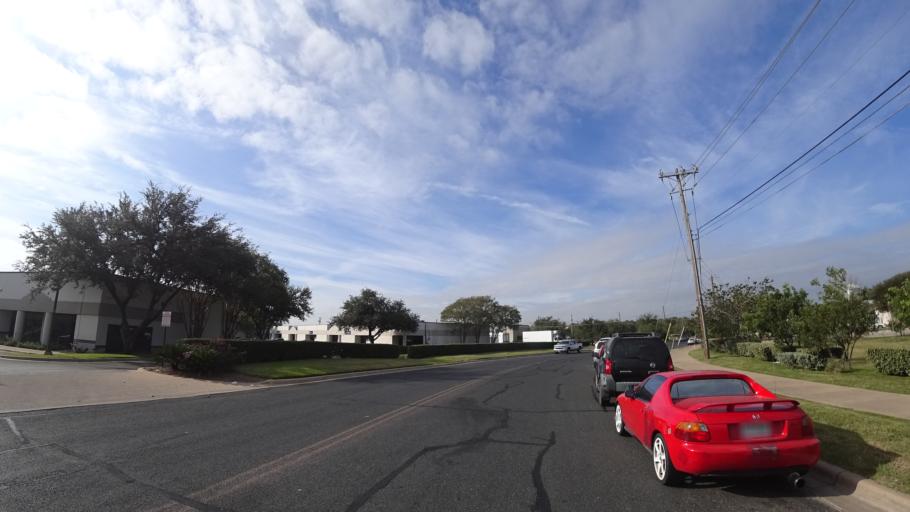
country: US
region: Texas
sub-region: Travis County
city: Austin
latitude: 30.2102
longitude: -97.7271
